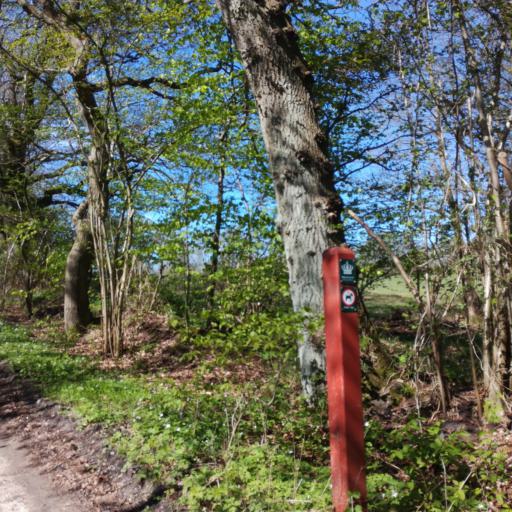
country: DK
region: South Denmark
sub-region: Vejle Kommune
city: Borkop
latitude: 55.6101
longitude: 9.6903
